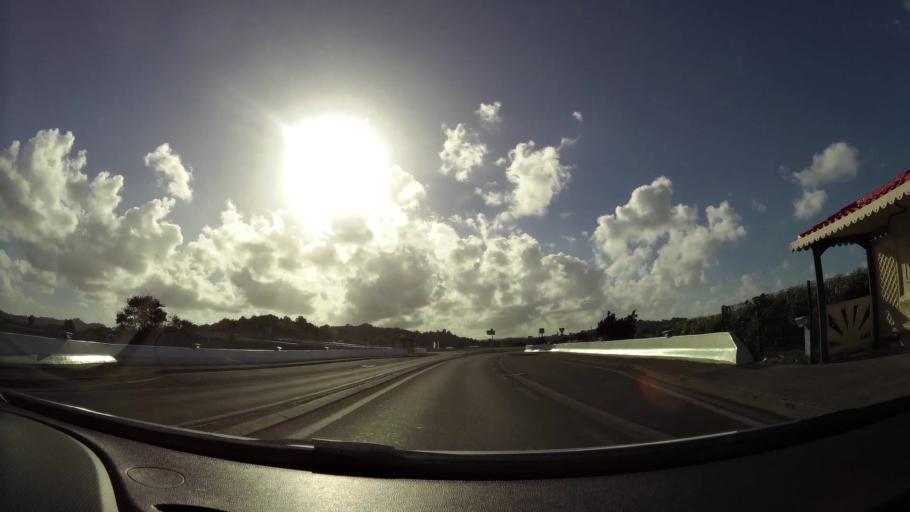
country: MQ
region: Martinique
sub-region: Martinique
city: Ducos
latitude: 14.5942
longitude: -60.9852
